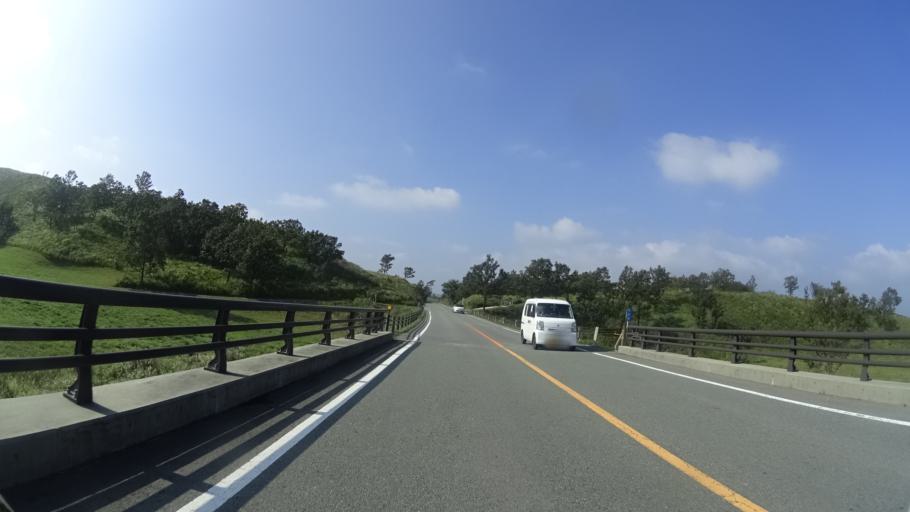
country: JP
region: Kumamoto
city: Aso
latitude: 33.0249
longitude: 131.0674
